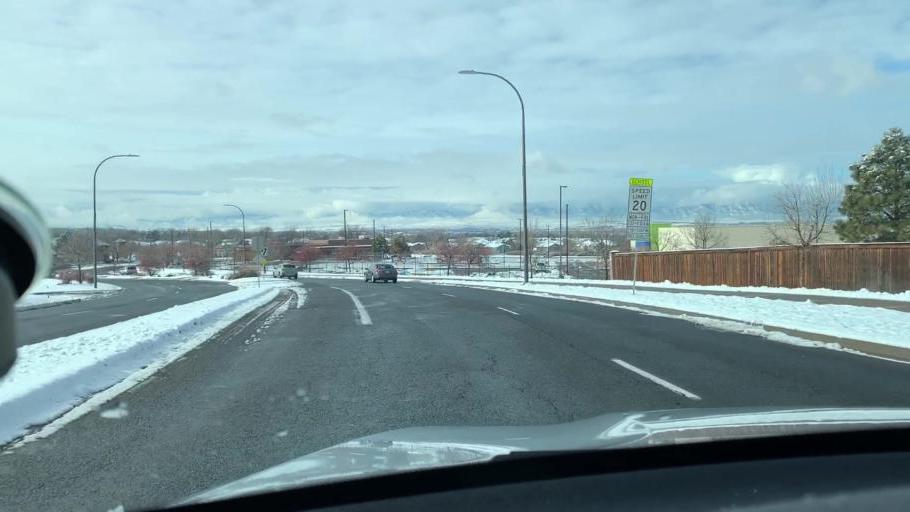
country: US
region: Colorado
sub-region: Adams County
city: Northglenn
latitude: 39.9006
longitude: -104.9924
